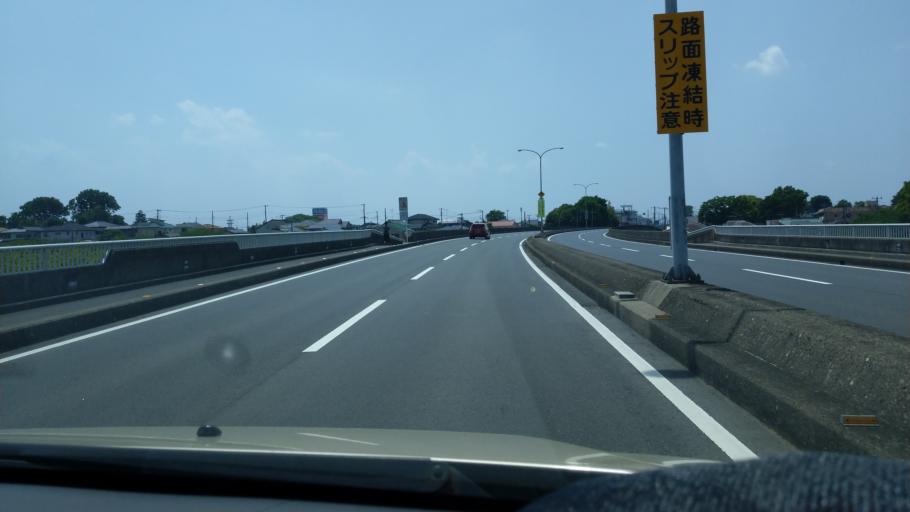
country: JP
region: Saitama
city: Saitama
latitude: 35.8824
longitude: 139.6980
